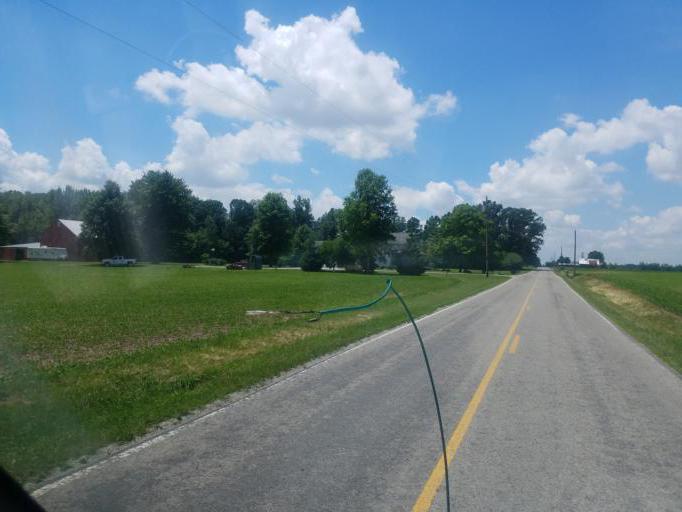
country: US
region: Ohio
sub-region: Huron County
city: Plymouth
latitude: 41.0680
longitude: -82.6326
